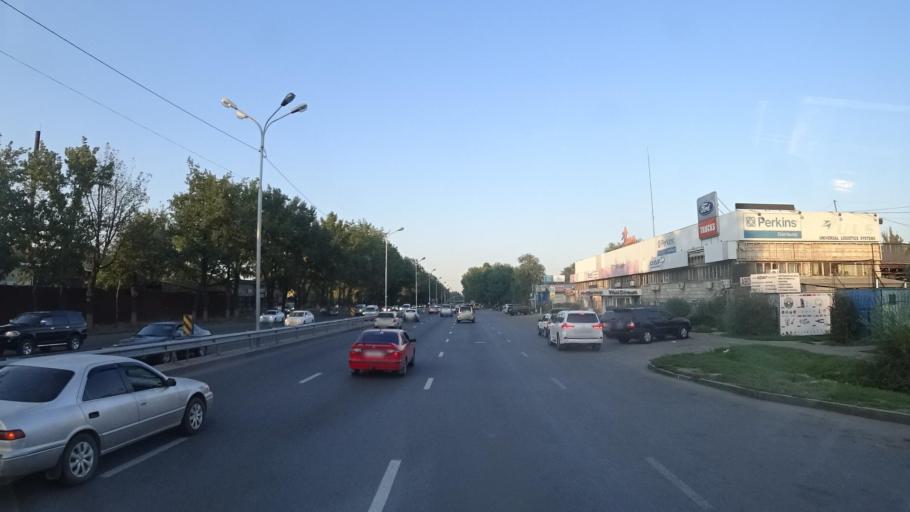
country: KZ
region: Almaty Qalasy
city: Almaty
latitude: 43.2844
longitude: 76.9193
